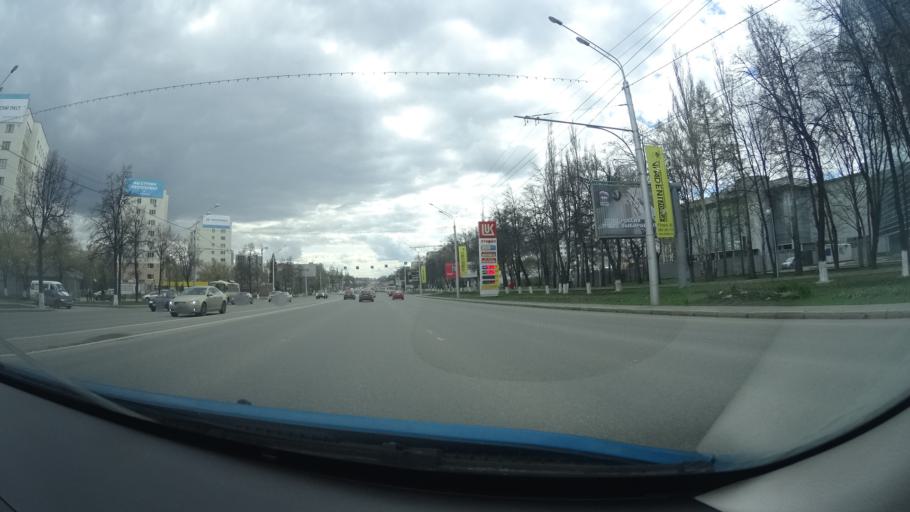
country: RU
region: Bashkortostan
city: Ufa
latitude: 54.7623
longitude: 56.0131
